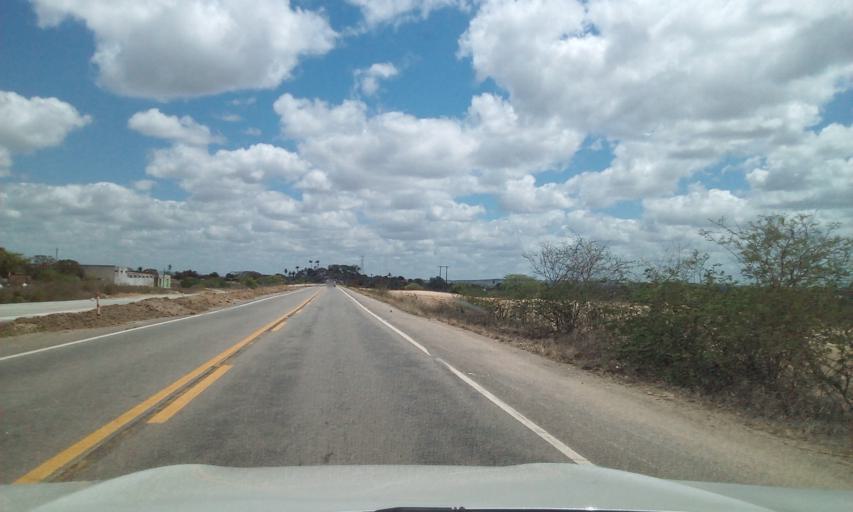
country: BR
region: Sergipe
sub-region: Propria
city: Propria
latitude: -10.2225
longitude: -36.8304
